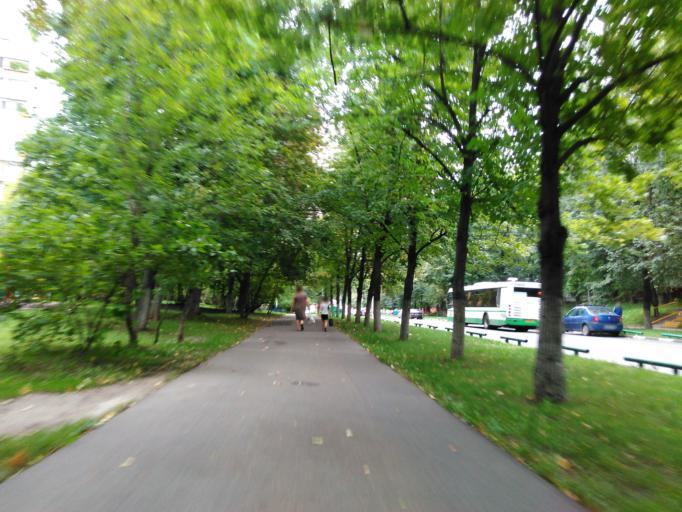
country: RU
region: Moscow
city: Kotlovka
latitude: 55.6615
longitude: 37.5860
